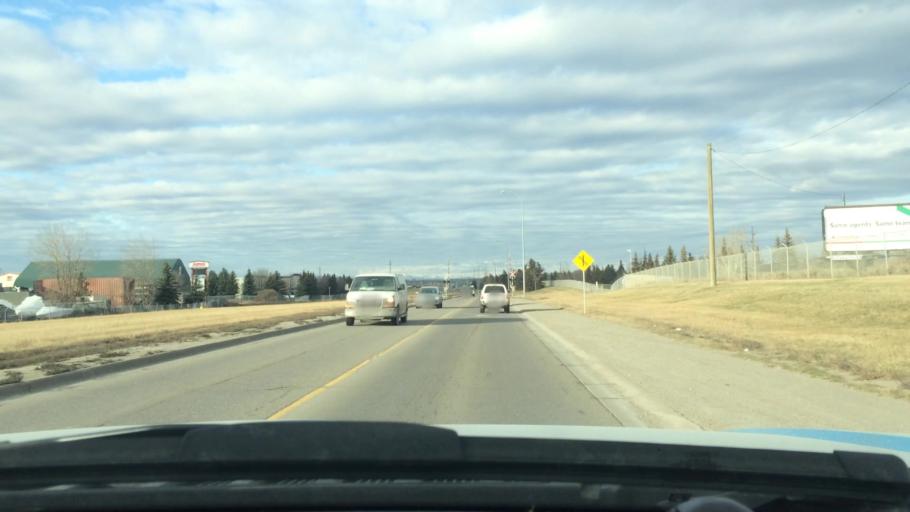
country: CA
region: Alberta
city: Calgary
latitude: 51.0153
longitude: -113.9837
